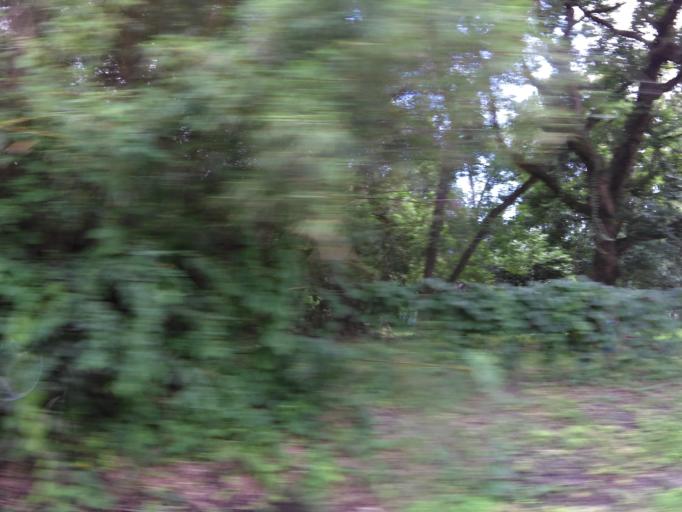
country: US
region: Florida
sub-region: Duval County
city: Jacksonville
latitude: 30.3621
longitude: -81.6820
